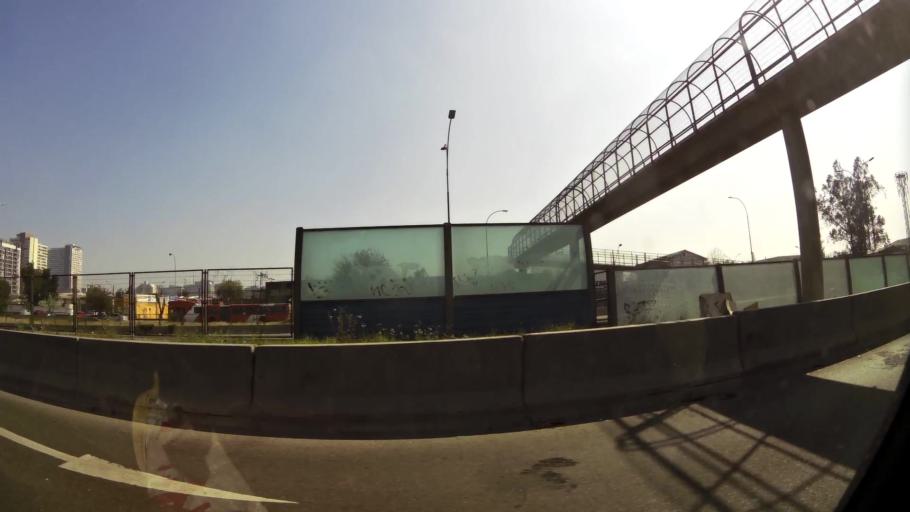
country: CL
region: Santiago Metropolitan
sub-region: Provincia de Santiago
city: Lo Prado
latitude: -33.4494
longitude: -70.6920
